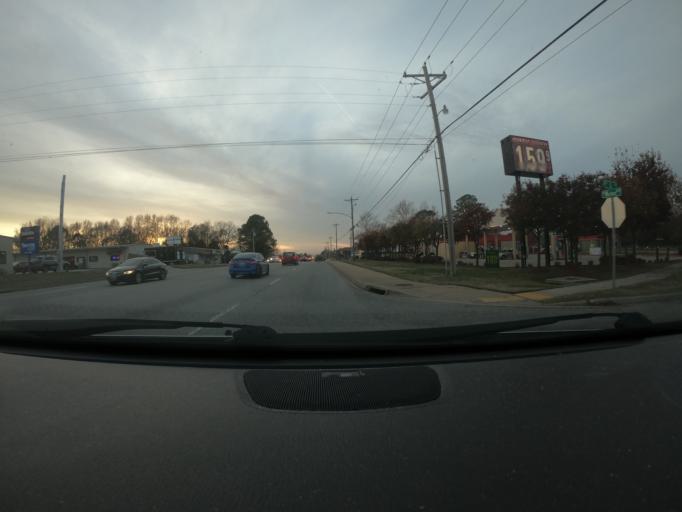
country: US
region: Arkansas
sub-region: Benton County
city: Bentonville
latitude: 36.3353
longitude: -94.1939
